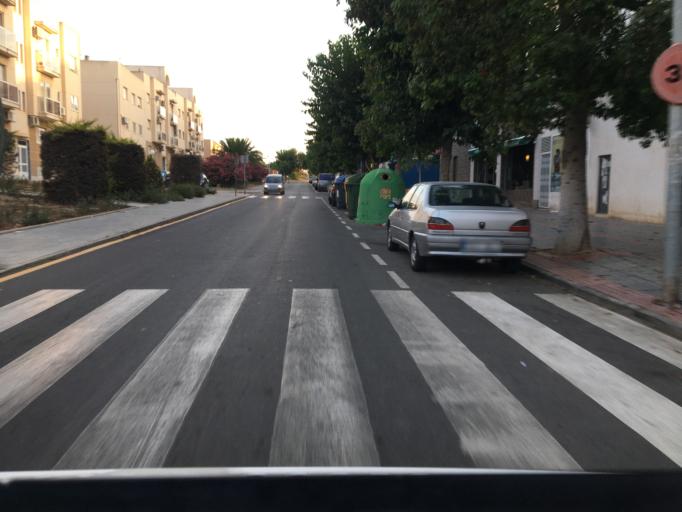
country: ES
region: Murcia
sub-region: Murcia
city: Cartagena
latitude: 37.6256
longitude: -0.9834
